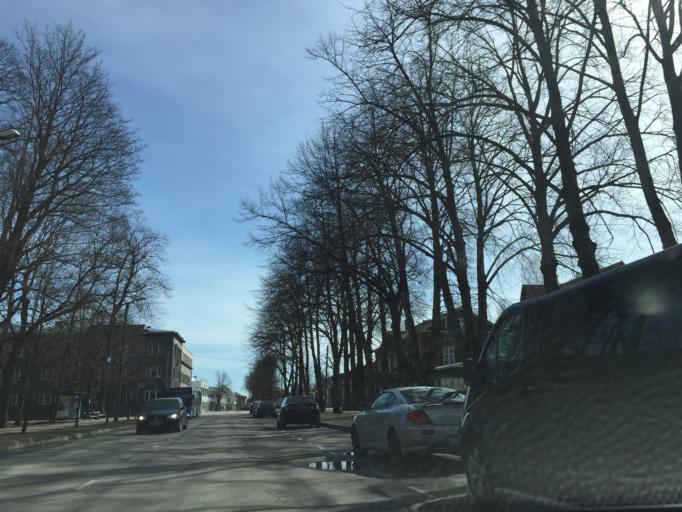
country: EE
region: Paernumaa
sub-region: Paernu linn
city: Parnu
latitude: 58.3830
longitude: 24.5080
